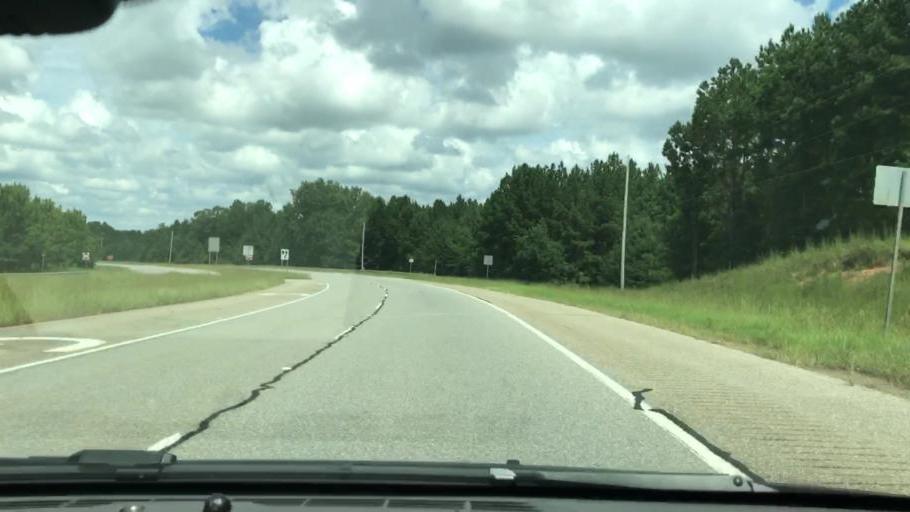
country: US
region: Georgia
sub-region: Stewart County
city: Lumpkin
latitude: 32.1168
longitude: -84.8143
